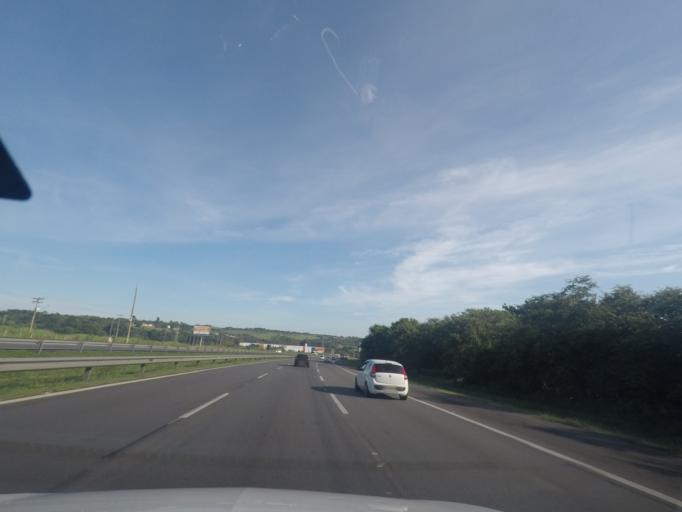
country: BR
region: Sao Paulo
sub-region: Americana
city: Americana
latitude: -22.6958
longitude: -47.3100
